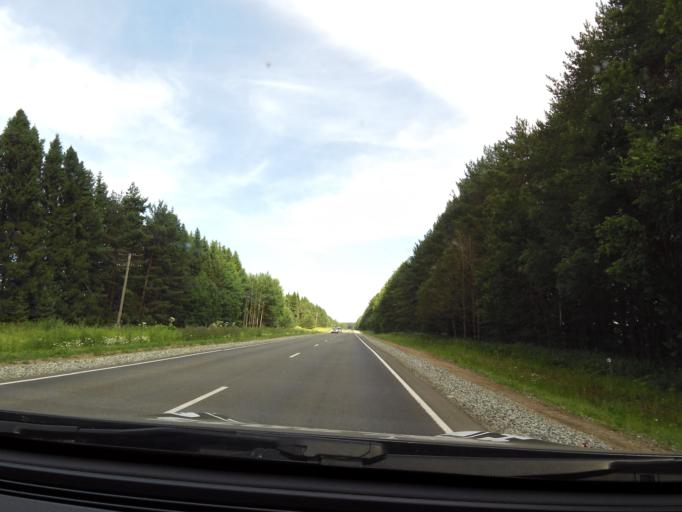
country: RU
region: Kirov
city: Slobodskoy
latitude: 58.7799
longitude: 50.4522
